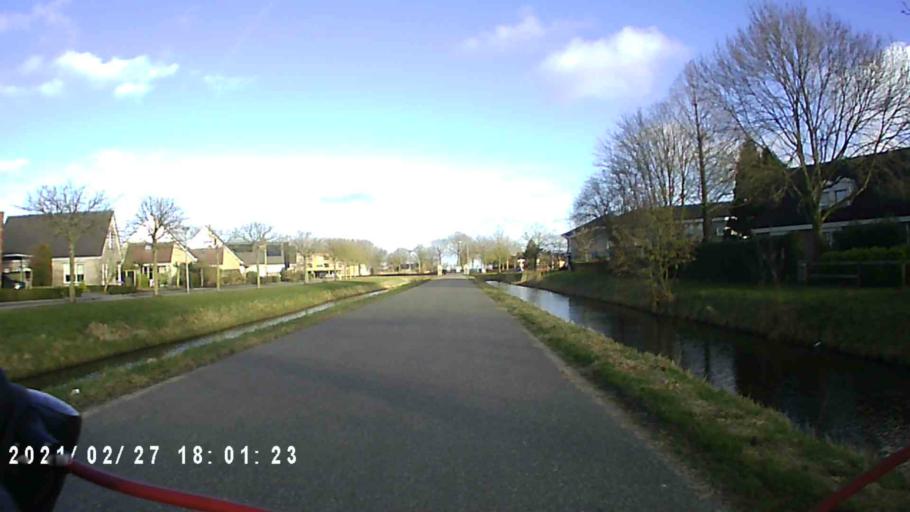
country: NL
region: Groningen
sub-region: Gemeente Bedum
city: Bedum
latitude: 53.3017
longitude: 6.6094
